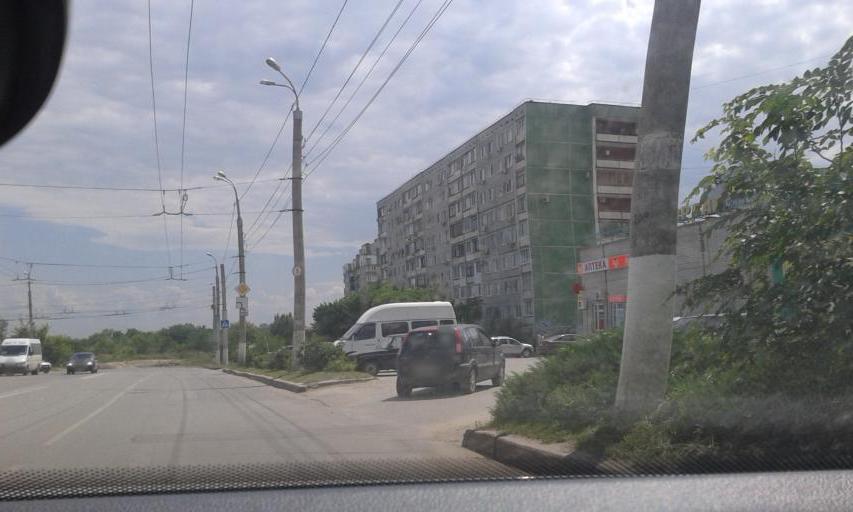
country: RU
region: Volgograd
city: Volgograd
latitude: 48.7561
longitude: 44.5111
